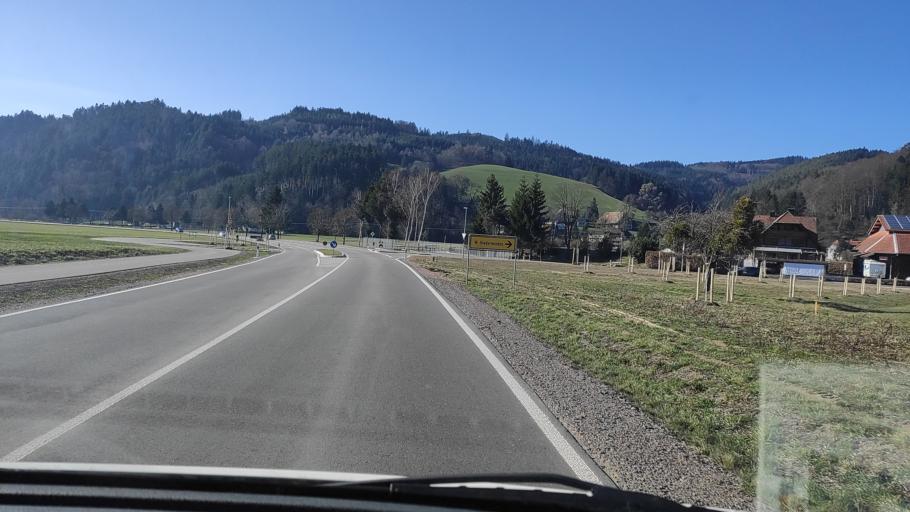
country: DE
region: Baden-Wuerttemberg
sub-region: Freiburg Region
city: Gutach im Breisgau
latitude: 48.1374
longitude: 8.0163
